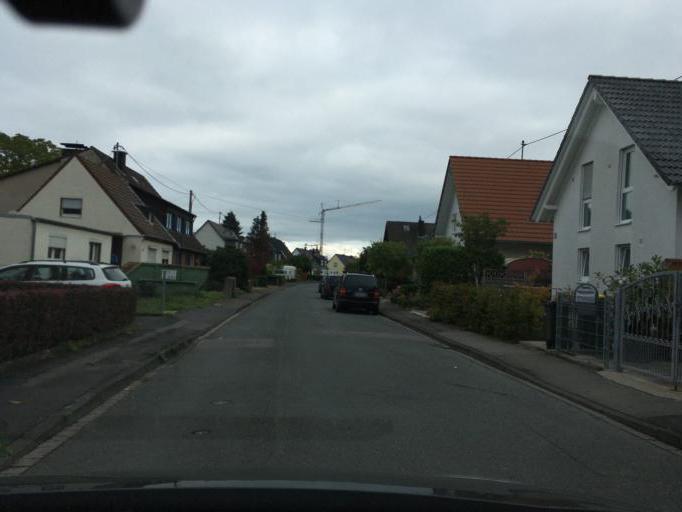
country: DE
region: North Rhine-Westphalia
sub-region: Regierungsbezirk Koln
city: Bonn
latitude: 50.7484
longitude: 7.1328
